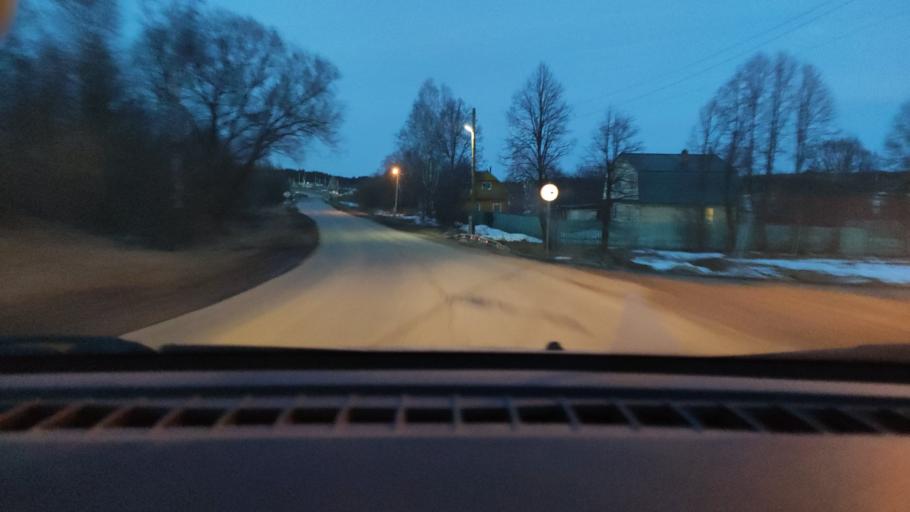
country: RU
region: Perm
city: Yug
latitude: 57.7289
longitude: 56.1985
